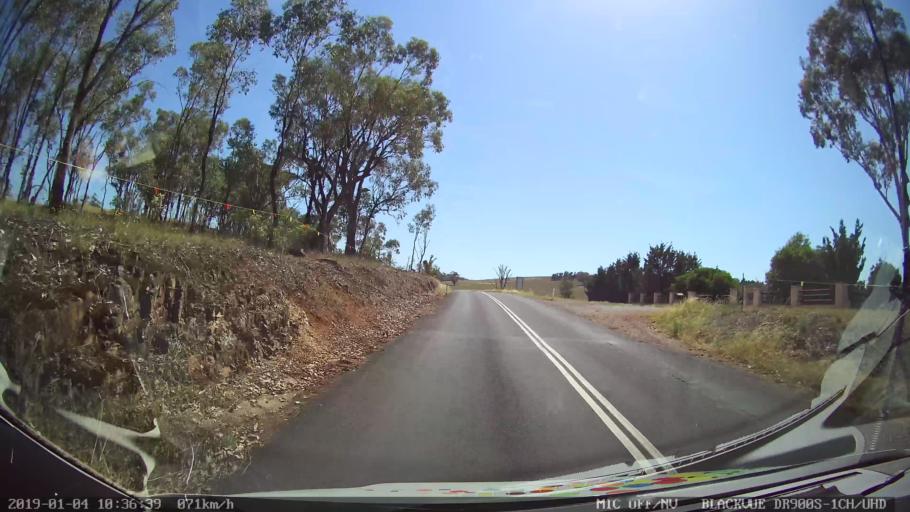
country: AU
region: New South Wales
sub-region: Cabonne
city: Canowindra
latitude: -33.3021
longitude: 148.6867
